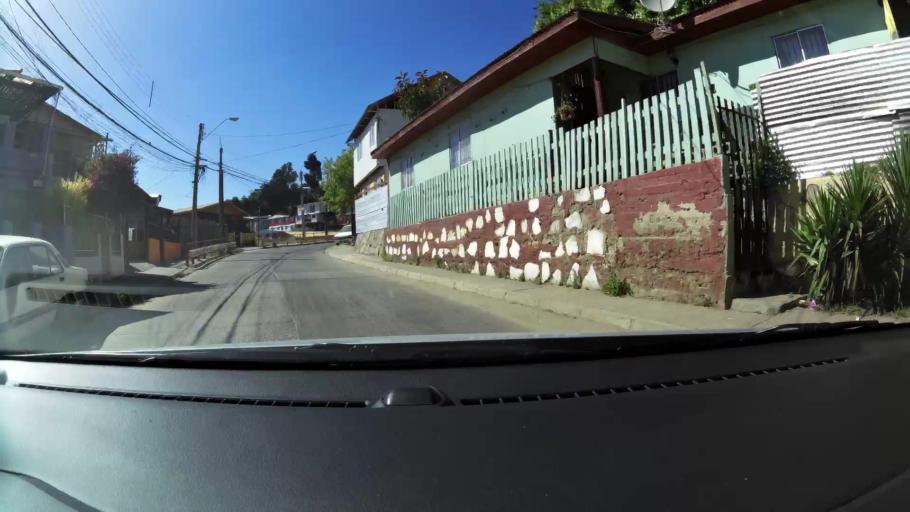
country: CL
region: Valparaiso
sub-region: Provincia de Valparaiso
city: Valparaiso
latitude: -33.0630
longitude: -71.5930
